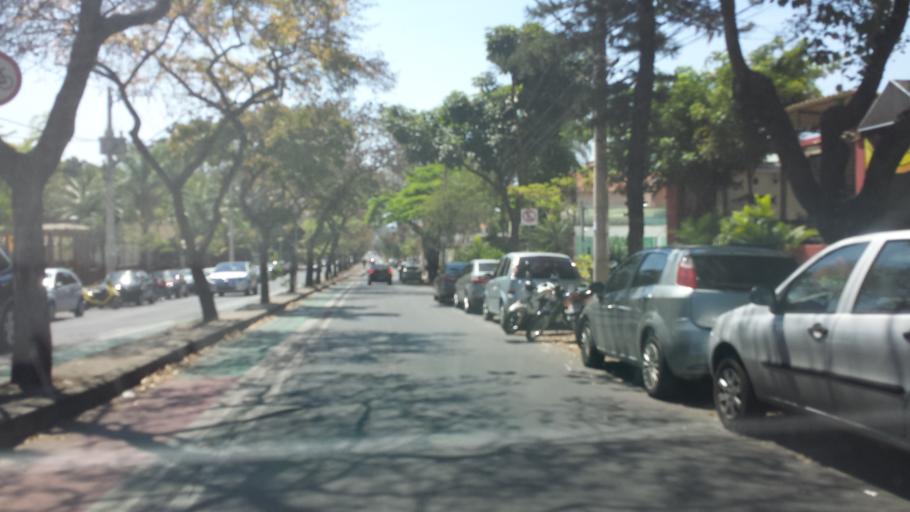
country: BR
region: Minas Gerais
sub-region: Belo Horizonte
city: Belo Horizonte
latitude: -19.8725
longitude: -43.9871
